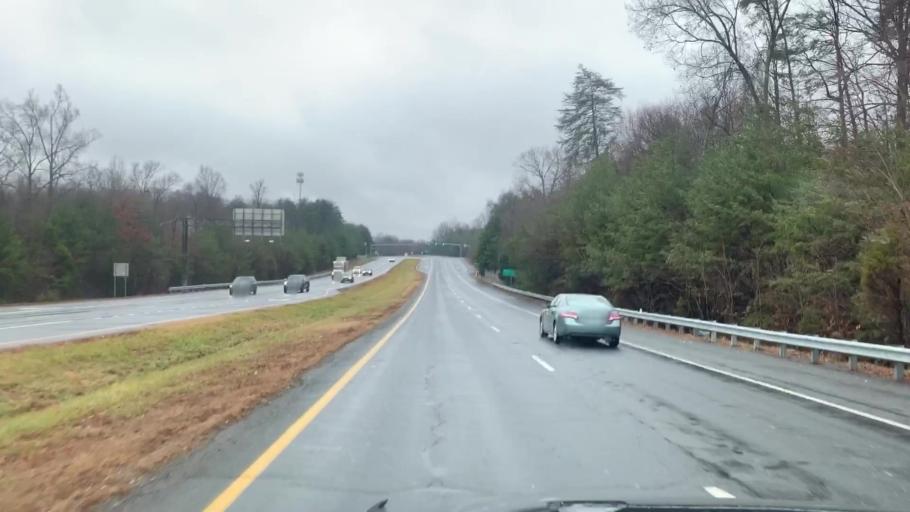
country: US
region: Virginia
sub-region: Fairfax County
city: Fairfax Station
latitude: 38.7854
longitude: -77.3273
